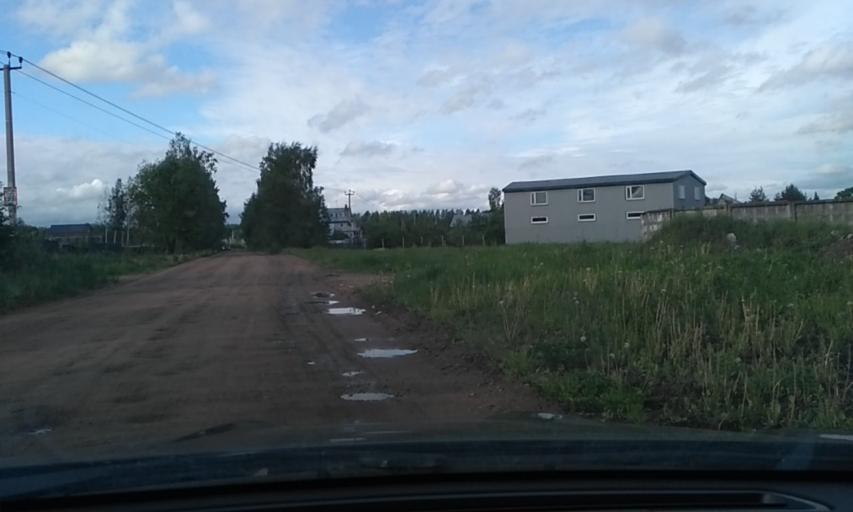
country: RU
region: Leningrad
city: Otradnoye
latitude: 59.8004
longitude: 30.8020
